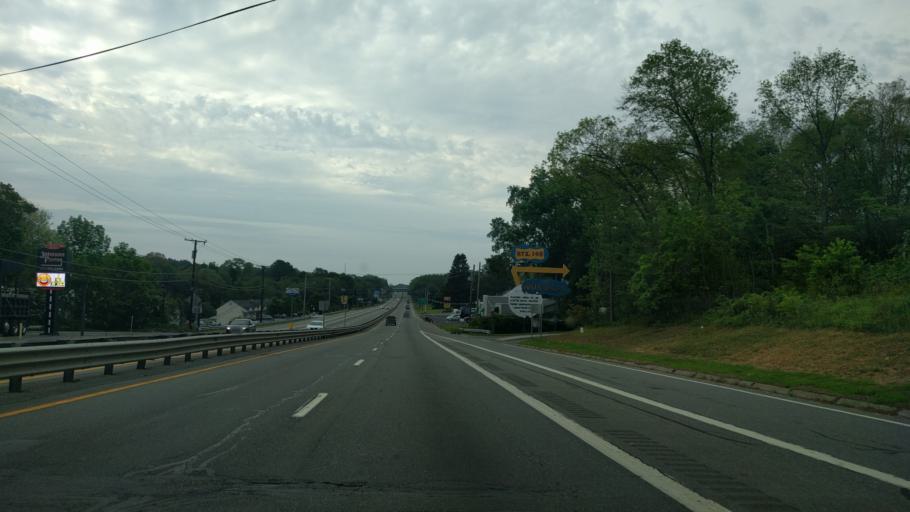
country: US
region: Rhode Island
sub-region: Providence County
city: Cumberland Hill
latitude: 41.9583
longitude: -71.4921
